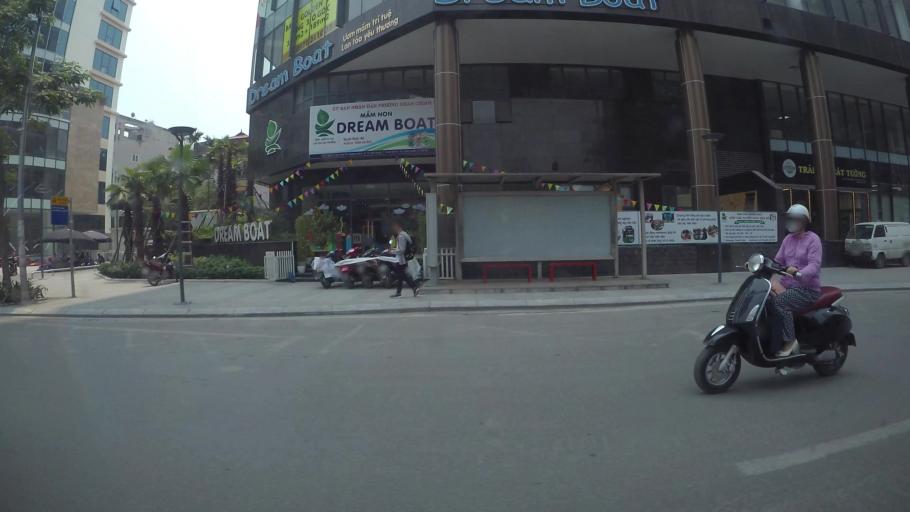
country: VN
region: Ha Noi
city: Thanh Xuan
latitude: 21.0074
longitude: 105.8080
